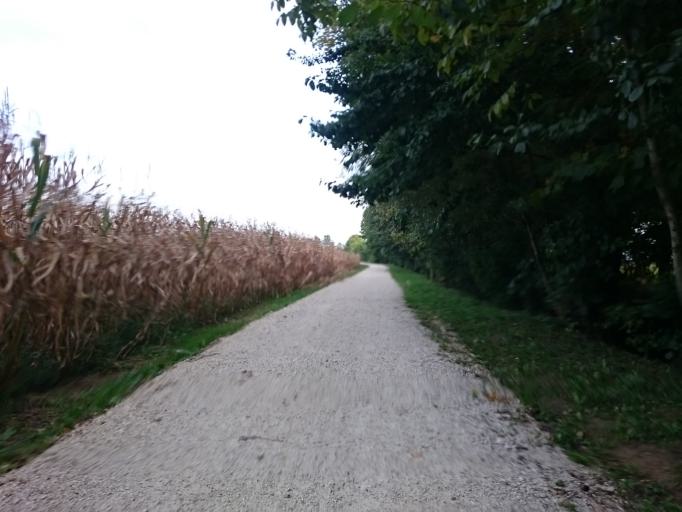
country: IT
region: Veneto
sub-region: Provincia di Vicenza
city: Grumolo delle Abbadesse
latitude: 45.5355
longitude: 11.6878
